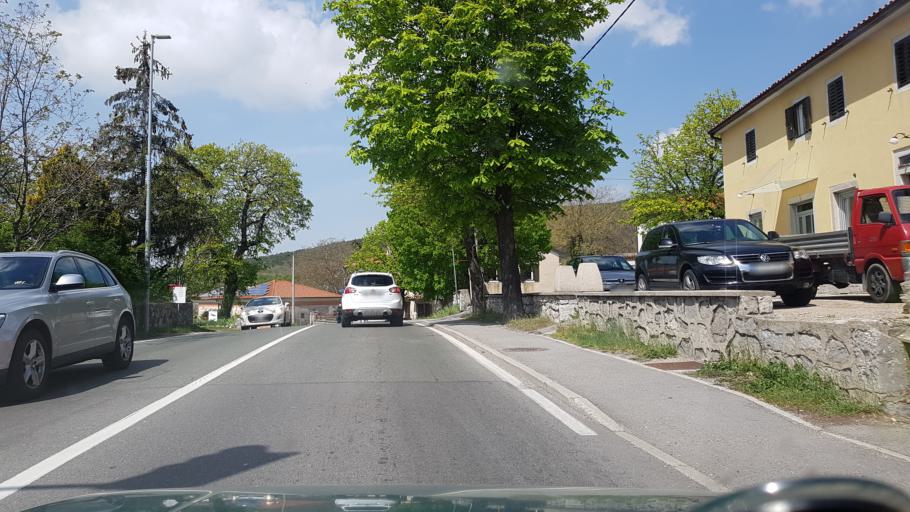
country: SI
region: Hrpelje-Kozina
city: Kozina
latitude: 45.6092
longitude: 13.9377
